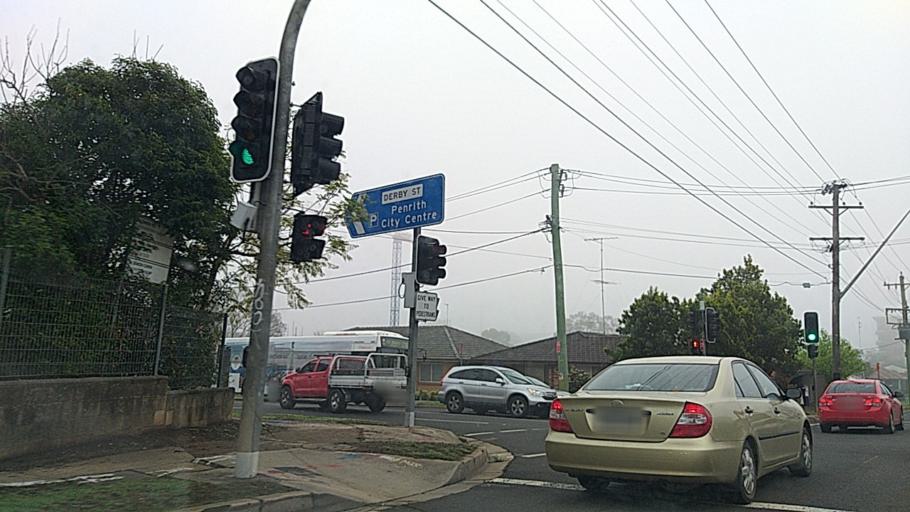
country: AU
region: New South Wales
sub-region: Penrith Municipality
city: Kingswood Park
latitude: -33.7608
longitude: 150.7108
